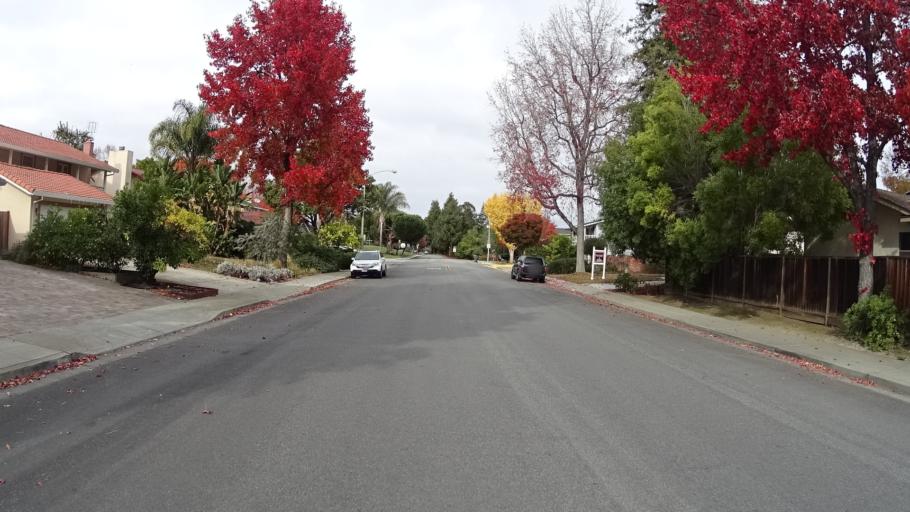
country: US
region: California
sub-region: Santa Clara County
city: Sunnyvale
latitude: 37.3615
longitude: -122.0370
